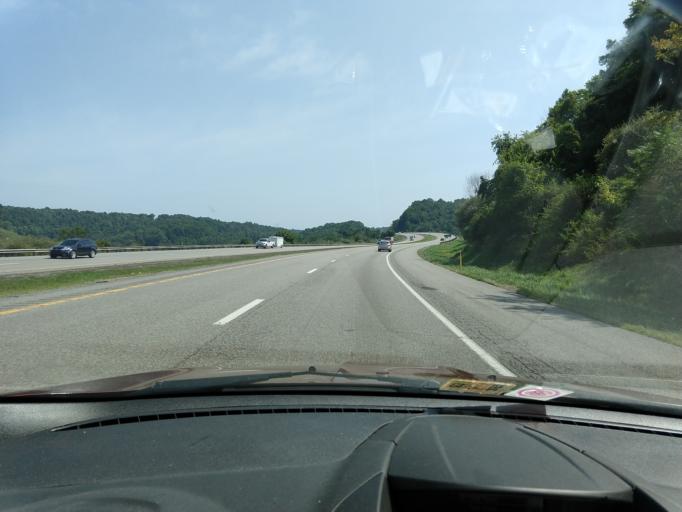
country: US
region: West Virginia
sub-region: Lewis County
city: Weston
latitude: 39.0442
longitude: -80.4143
